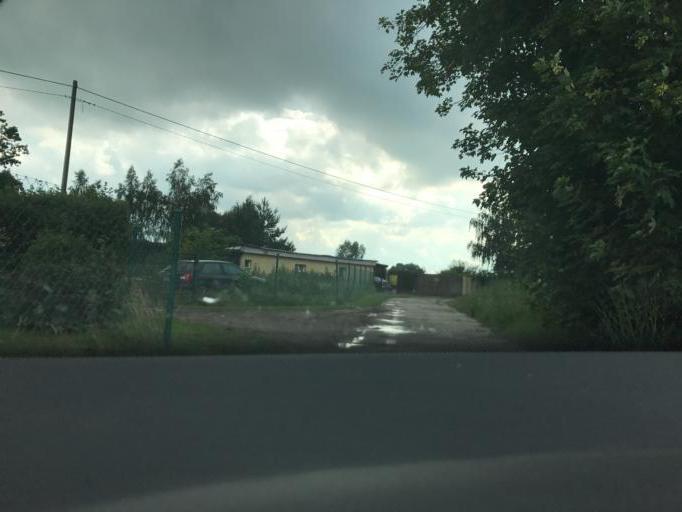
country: PL
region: Pomeranian Voivodeship
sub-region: Powiat gdanski
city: Cedry Wielkie
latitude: 54.3393
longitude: 18.8165
